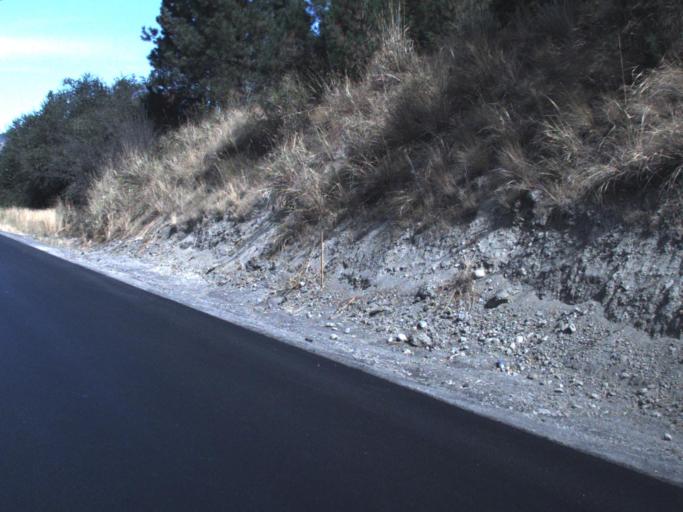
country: US
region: Washington
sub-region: Stevens County
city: Colville
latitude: 48.4880
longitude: -117.9026
